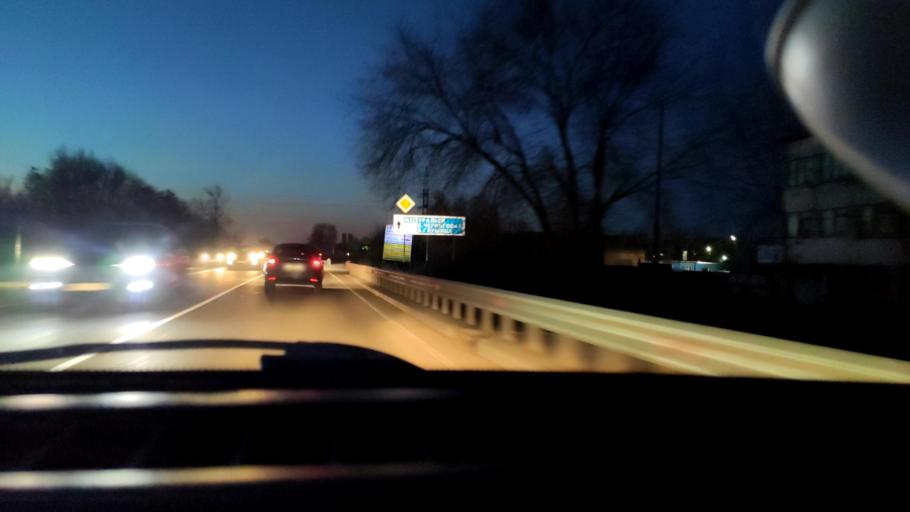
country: RU
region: Samara
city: Samara
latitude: 53.1315
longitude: 50.1077
